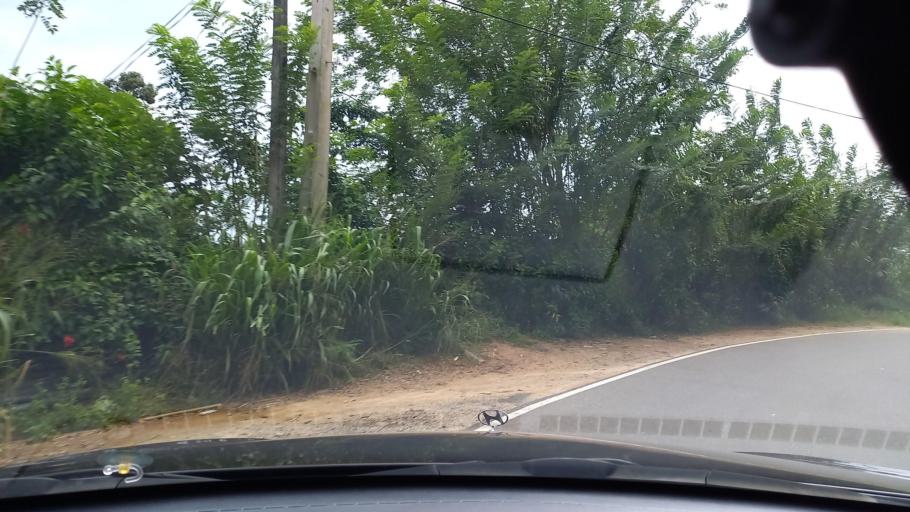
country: LK
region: Central
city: Gampola
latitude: 7.2117
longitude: 80.6165
